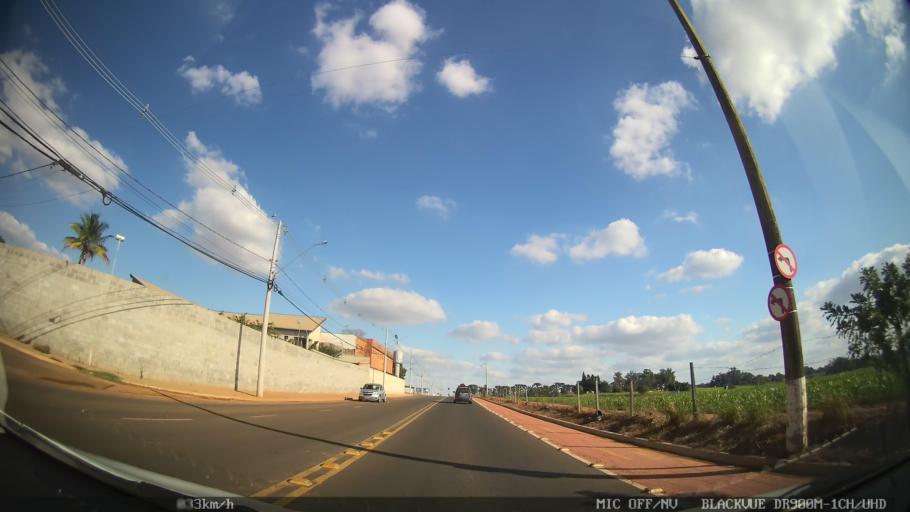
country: BR
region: Sao Paulo
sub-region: Nova Odessa
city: Nova Odessa
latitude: -22.8083
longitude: -47.3200
